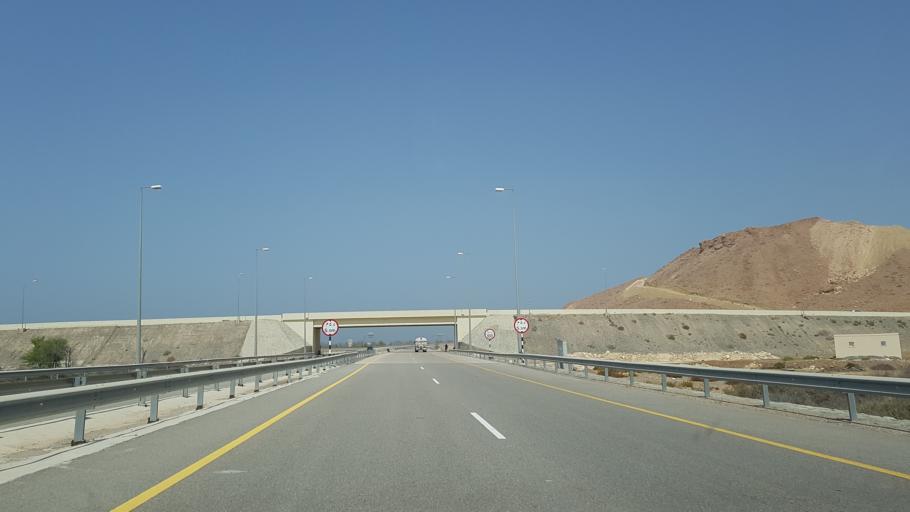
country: OM
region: Muhafazat Masqat
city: Muscat
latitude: 23.2106
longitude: 58.9252
